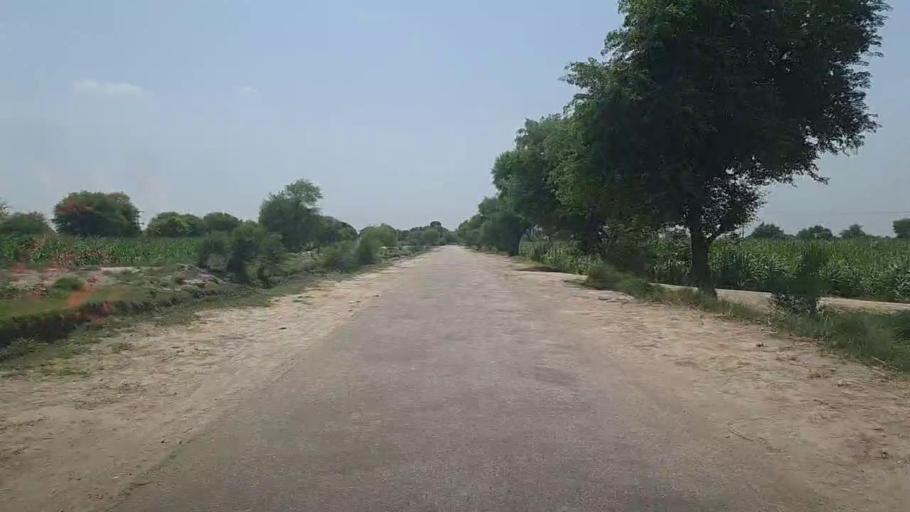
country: PK
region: Sindh
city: Ubauro
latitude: 28.2895
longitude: 69.8086
